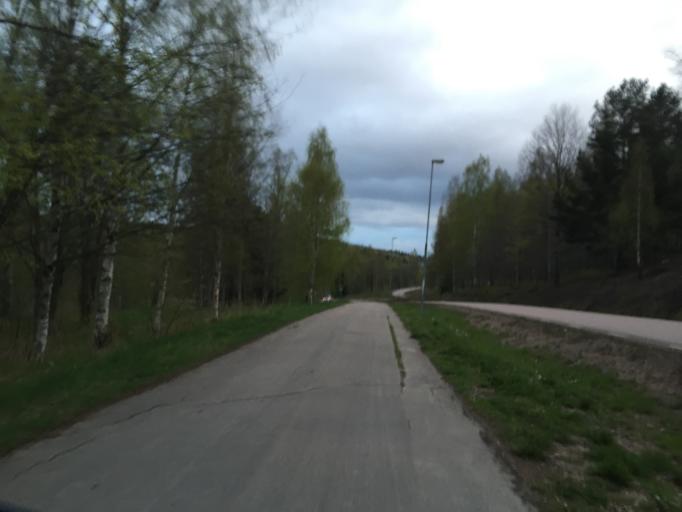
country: SE
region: Dalarna
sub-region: Ludvika Kommun
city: Ludvika
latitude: 60.1377
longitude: 15.1985
